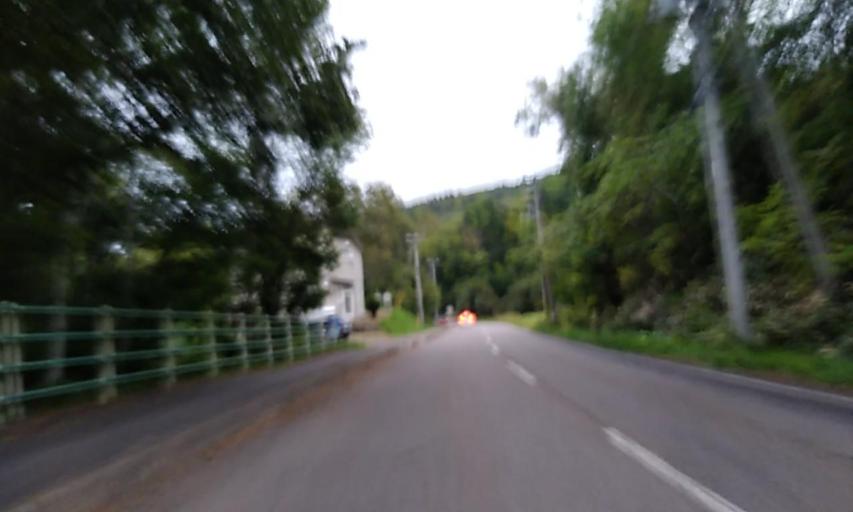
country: JP
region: Hokkaido
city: Abashiri
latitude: 44.0012
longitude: 144.2300
